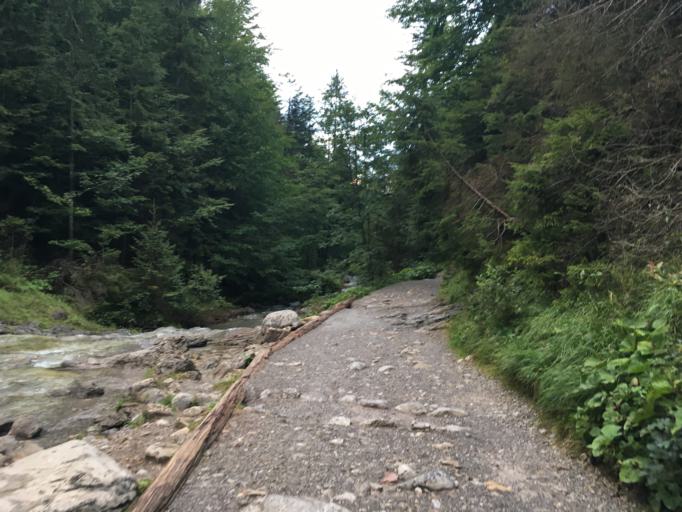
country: PL
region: Lesser Poland Voivodeship
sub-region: Powiat tatrzanski
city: Zakopane
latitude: 49.2730
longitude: 19.9330
